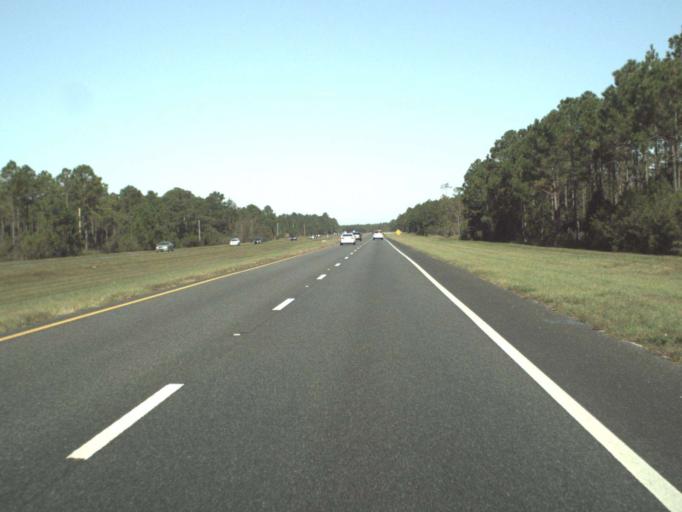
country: US
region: Florida
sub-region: Walton County
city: Seaside
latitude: 30.3192
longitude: -86.0448
